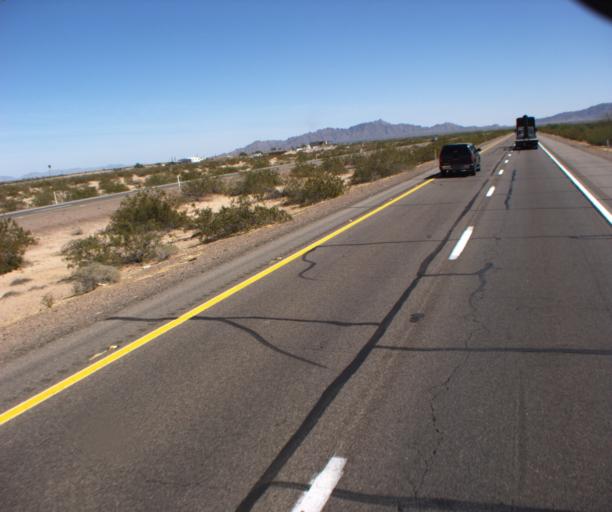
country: US
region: Arizona
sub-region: Yuma County
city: Wellton
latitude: 32.7010
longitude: -113.9030
